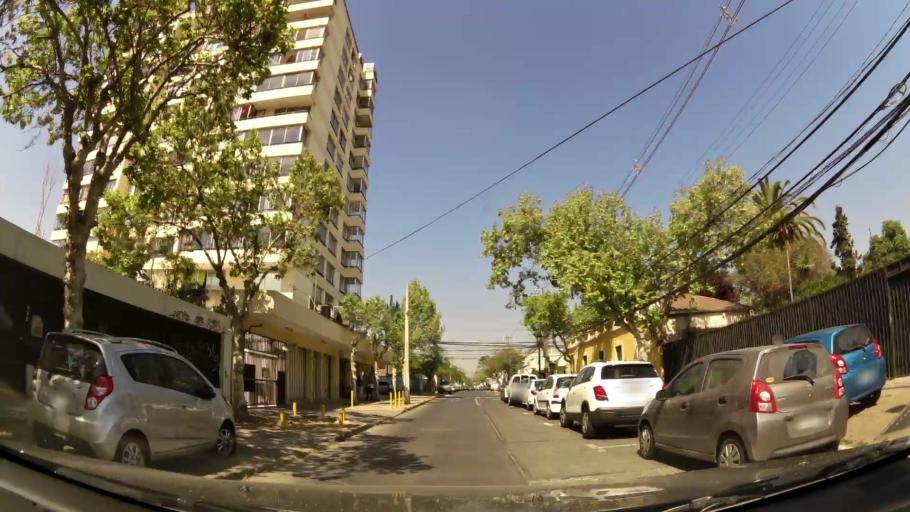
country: CL
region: Santiago Metropolitan
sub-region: Provincia de Maipo
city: San Bernardo
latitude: -33.5932
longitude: -70.7012
